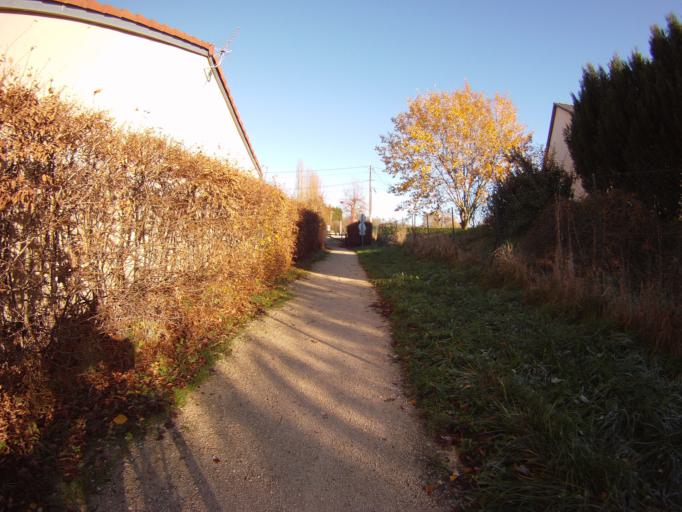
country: FR
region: Lorraine
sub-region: Departement de Meurthe-et-Moselle
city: Bouxieres-aux-Chenes
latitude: 48.7941
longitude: 6.2335
